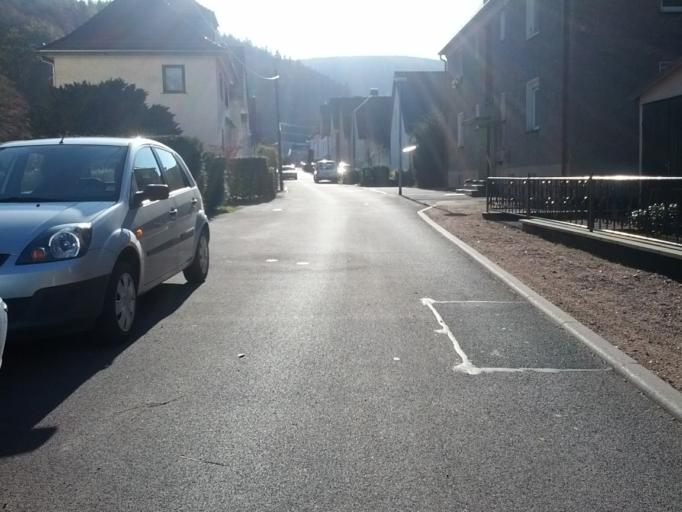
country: DE
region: Thuringia
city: Thal
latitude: 50.9156
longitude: 10.3903
